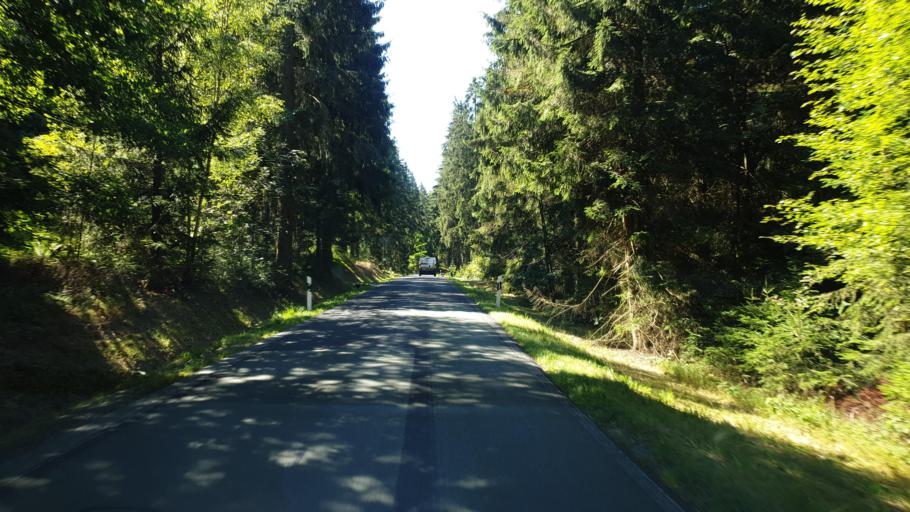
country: DE
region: Saxony
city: Auerbach
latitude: 50.4843
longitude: 12.4375
